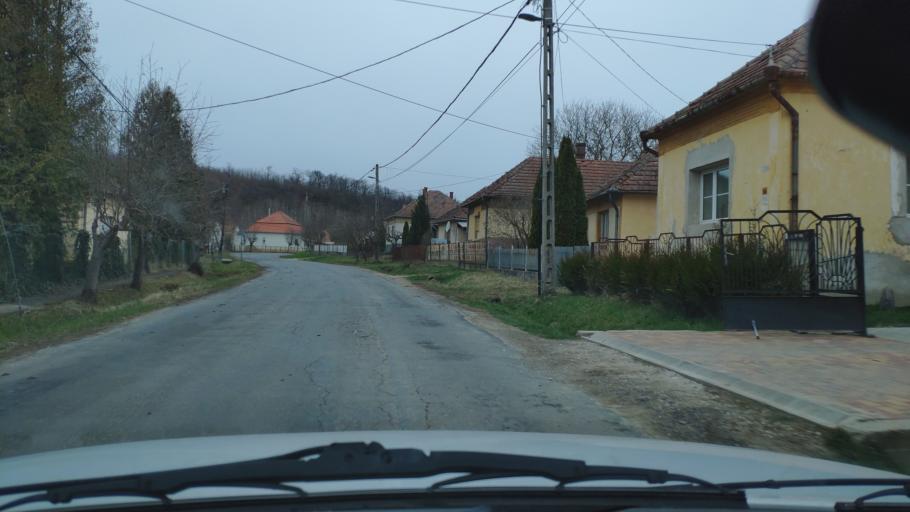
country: HU
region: Zala
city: Pacsa
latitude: 46.6762
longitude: 17.0539
